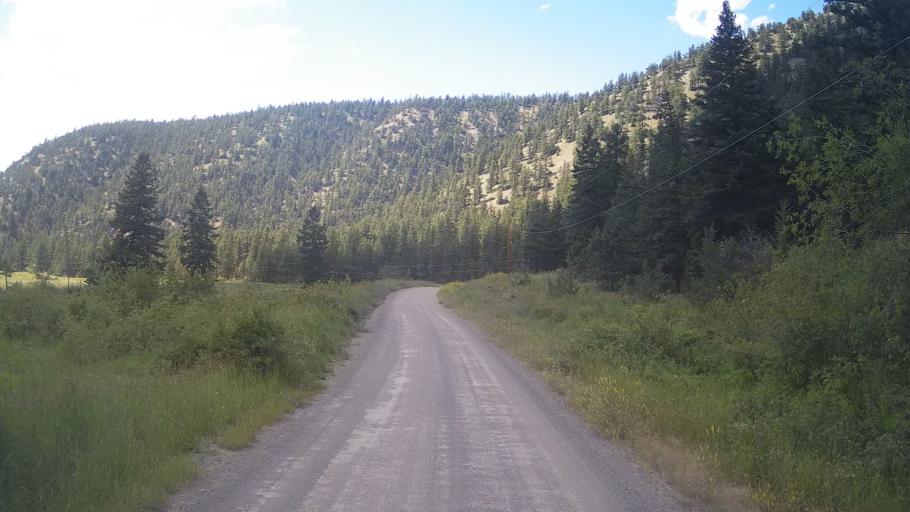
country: CA
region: British Columbia
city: Lillooet
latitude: 51.2514
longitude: -122.0175
